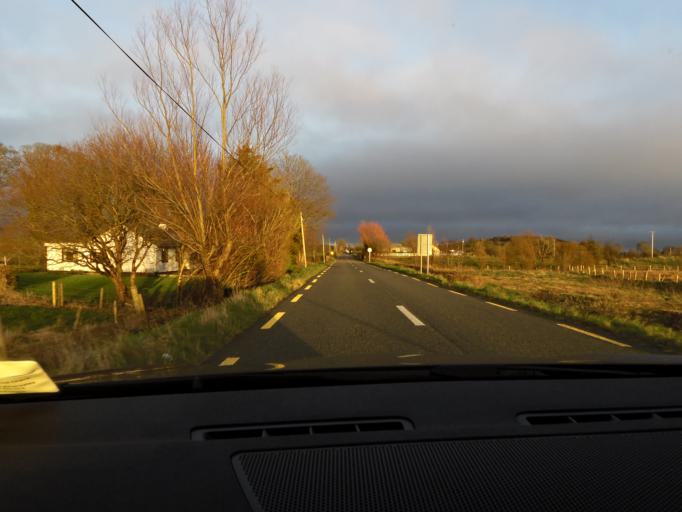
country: IE
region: Connaught
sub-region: Sligo
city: Ballymote
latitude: 54.0334
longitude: -8.5983
